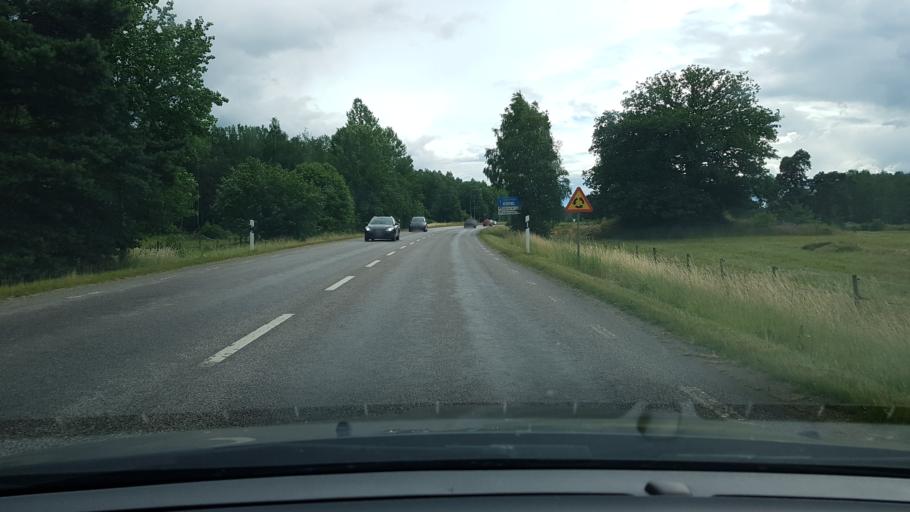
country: SE
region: Uppsala
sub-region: Uppsala Kommun
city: Saevja
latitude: 59.8194
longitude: 17.6987
